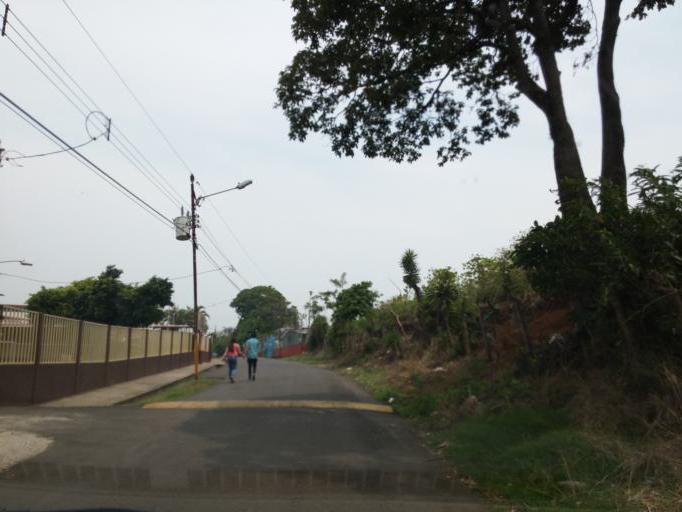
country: CR
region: Heredia
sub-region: Canton de Belen
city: San Antonio
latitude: 9.9927
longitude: -84.2005
